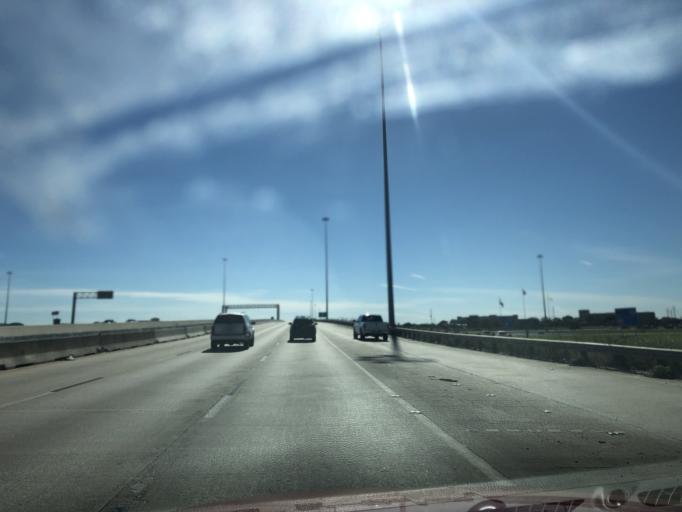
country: US
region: Texas
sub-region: Brazoria County
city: Brookside Village
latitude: 29.5837
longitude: -95.3866
